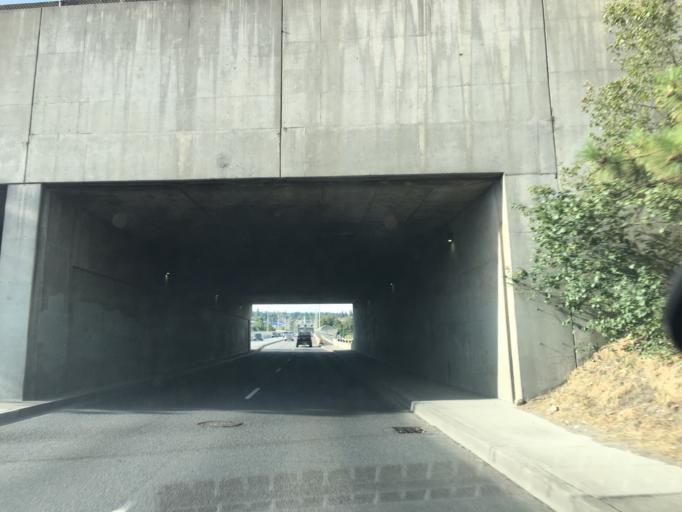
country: US
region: Washington
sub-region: Spokane County
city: Spokane
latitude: 47.6623
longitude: -117.4357
